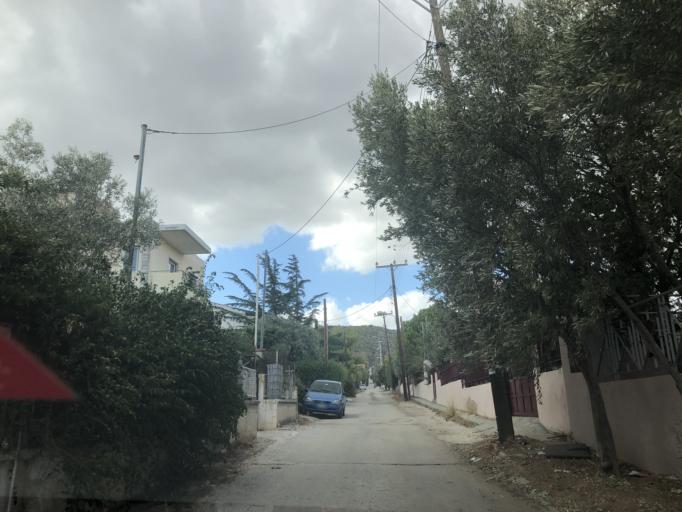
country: GR
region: Attica
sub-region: Nomarchia Anatolikis Attikis
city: Agia Marina
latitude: 37.8247
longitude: 23.8456
